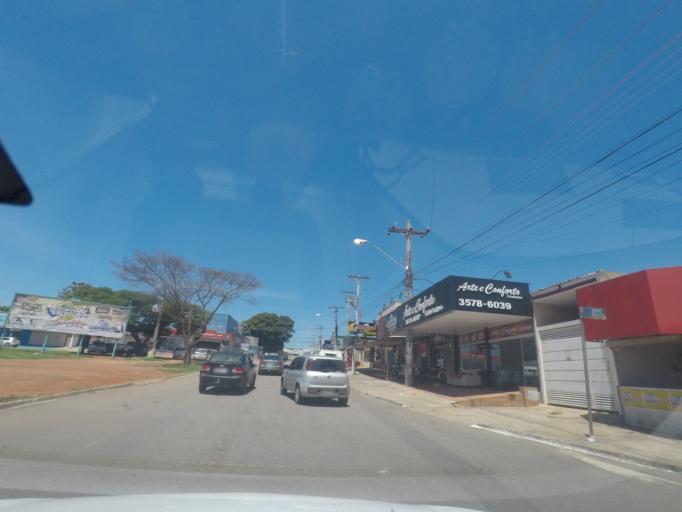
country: BR
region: Goias
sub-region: Aparecida De Goiania
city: Aparecida de Goiania
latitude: -16.7681
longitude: -49.3426
